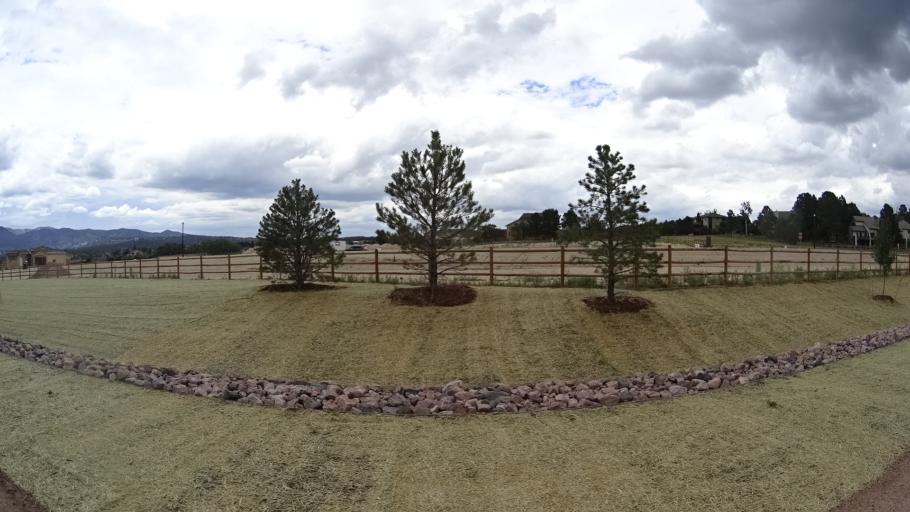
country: US
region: Colorado
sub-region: El Paso County
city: Woodmoor
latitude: 39.0976
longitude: -104.8539
